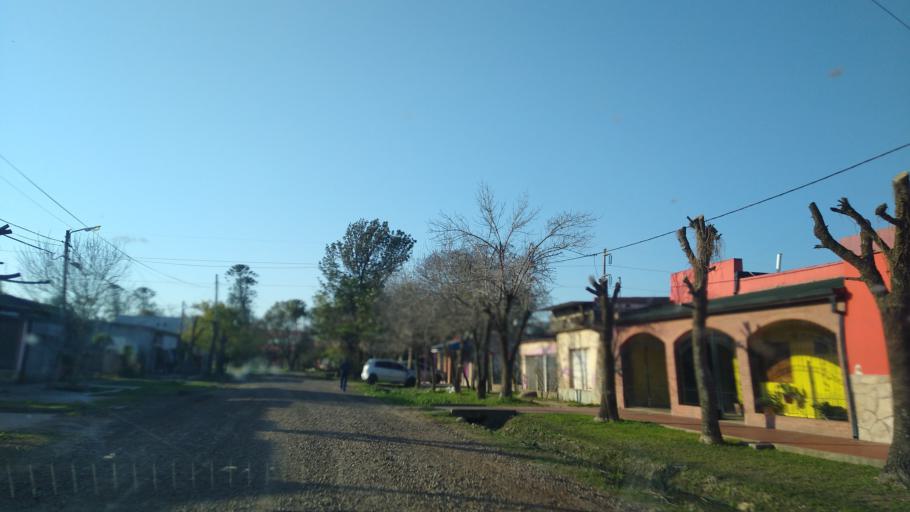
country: AR
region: Chaco
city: Barranqueras
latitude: -27.4895
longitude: -58.9451
